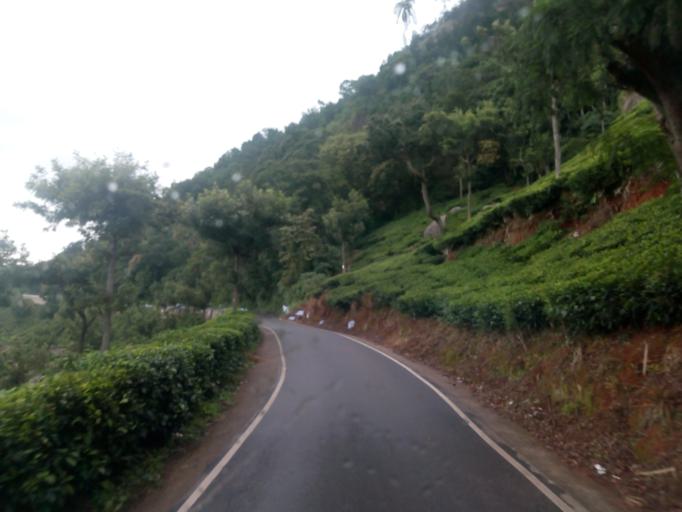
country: IN
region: Tamil Nadu
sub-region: Nilgiri
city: Kotagiri
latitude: 11.3645
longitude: 76.8527
